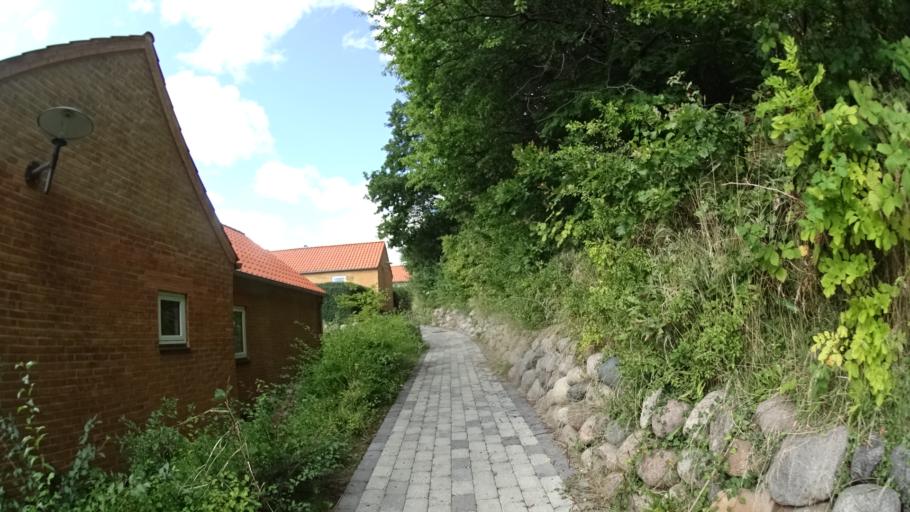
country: DK
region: Central Jutland
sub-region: Arhus Kommune
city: Arhus
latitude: 56.1136
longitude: 10.1878
